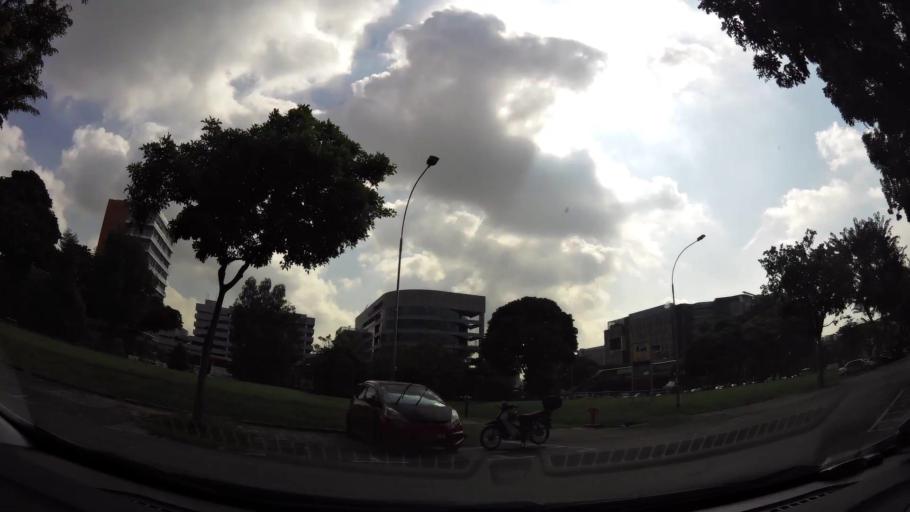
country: SG
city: Singapore
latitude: 1.3212
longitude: 103.8905
